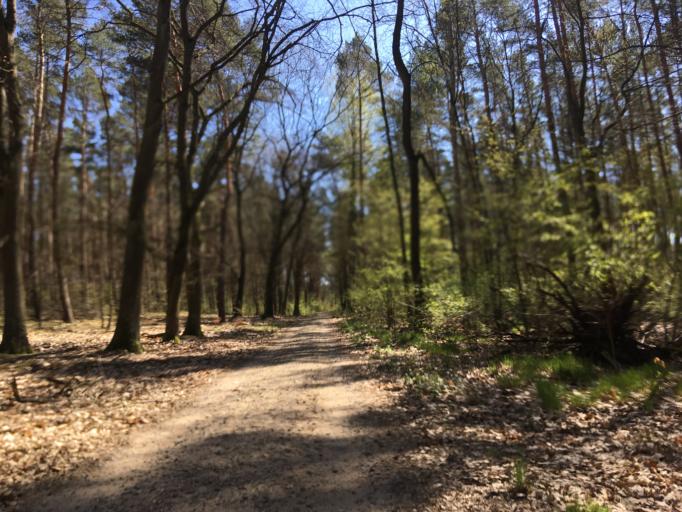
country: DE
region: Brandenburg
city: Bernau bei Berlin
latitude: 52.7000
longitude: 13.5371
